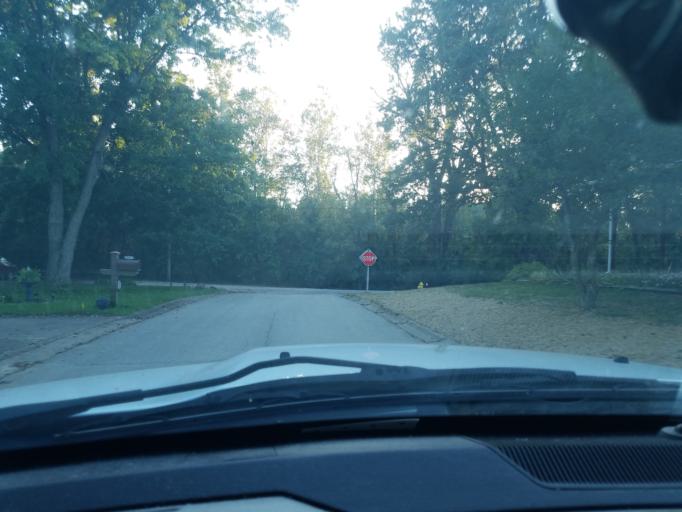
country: US
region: Indiana
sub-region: Floyd County
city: New Albany
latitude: 38.3406
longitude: -85.8109
